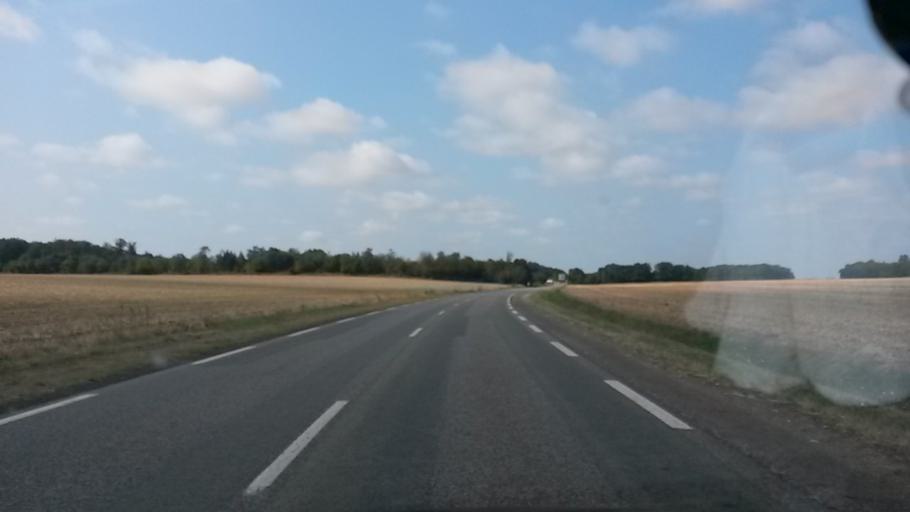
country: FR
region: Haute-Normandie
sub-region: Departement de l'Eure
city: Damville
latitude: 48.8287
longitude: 1.0170
